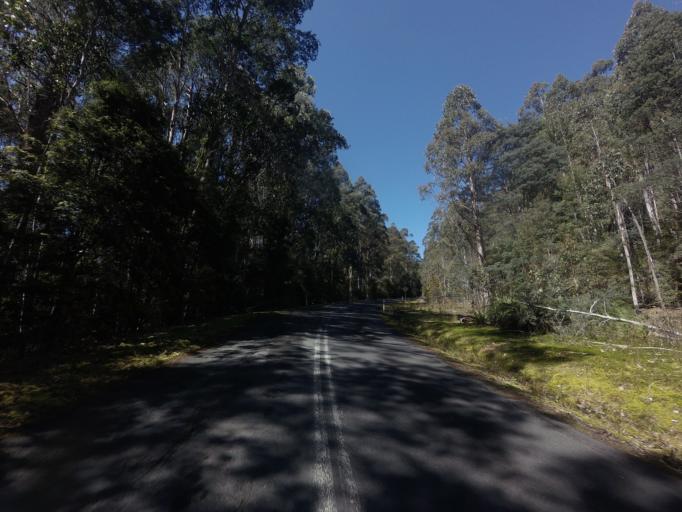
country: AU
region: Tasmania
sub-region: Huon Valley
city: Geeveston
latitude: -42.8163
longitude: 146.3462
